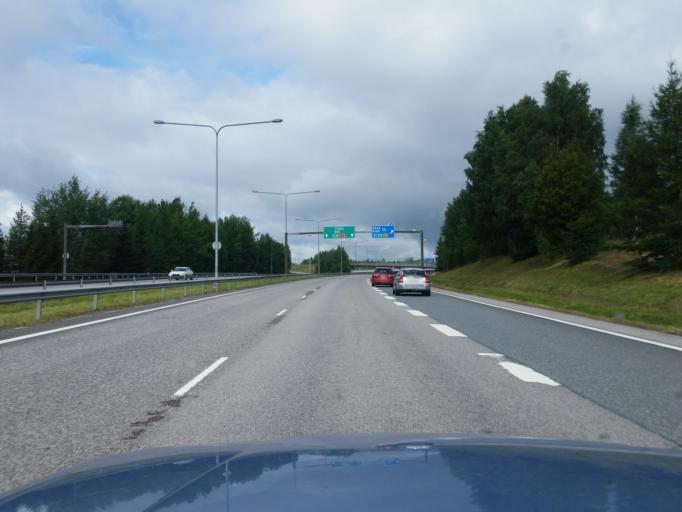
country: FI
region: Uusimaa
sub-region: Helsinki
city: Espoo
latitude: 60.2169
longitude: 24.6559
